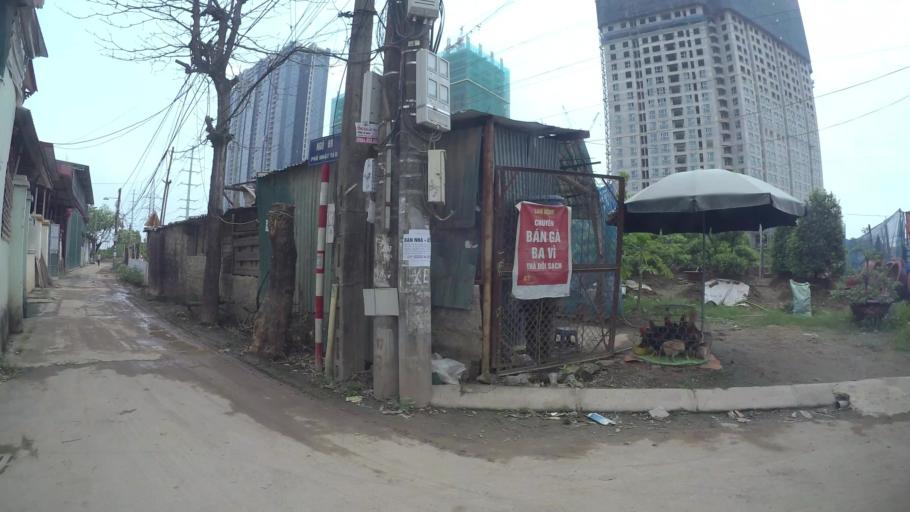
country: VN
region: Ha Noi
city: Tay Ho
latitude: 21.0872
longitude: 105.7886
